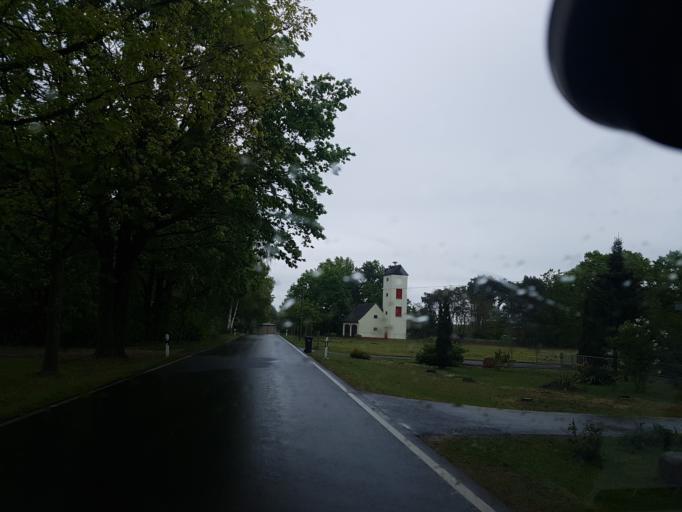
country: DE
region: Brandenburg
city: Spremberg
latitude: 51.6636
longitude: 14.4707
